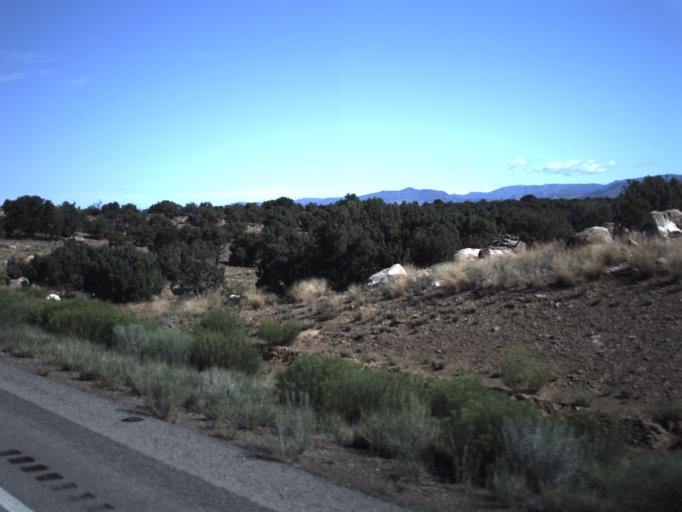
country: US
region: Utah
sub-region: Carbon County
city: East Carbon City
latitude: 39.4044
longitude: -110.4265
